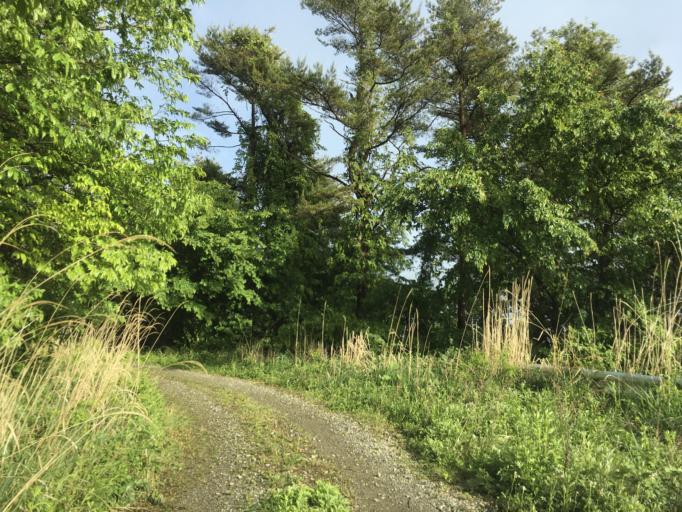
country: JP
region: Iwate
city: Ichinoseki
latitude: 38.8712
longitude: 141.4486
